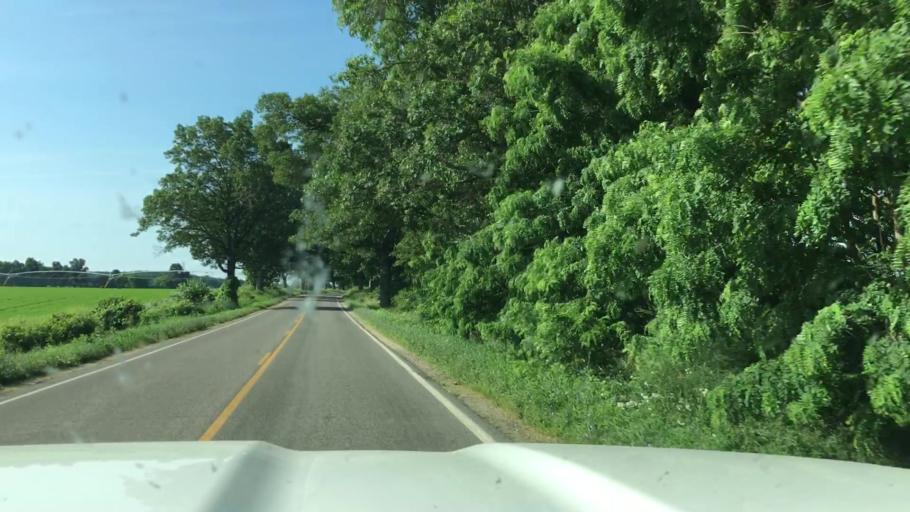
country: US
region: Michigan
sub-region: Barry County
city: Stony Point
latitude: 42.4514
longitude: -85.4545
